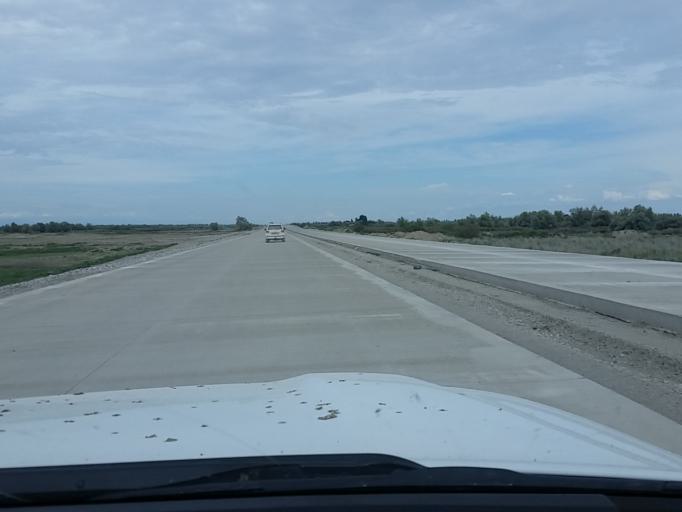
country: KZ
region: Almaty Oblysy
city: Zharkent
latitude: 44.0233
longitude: 79.8341
